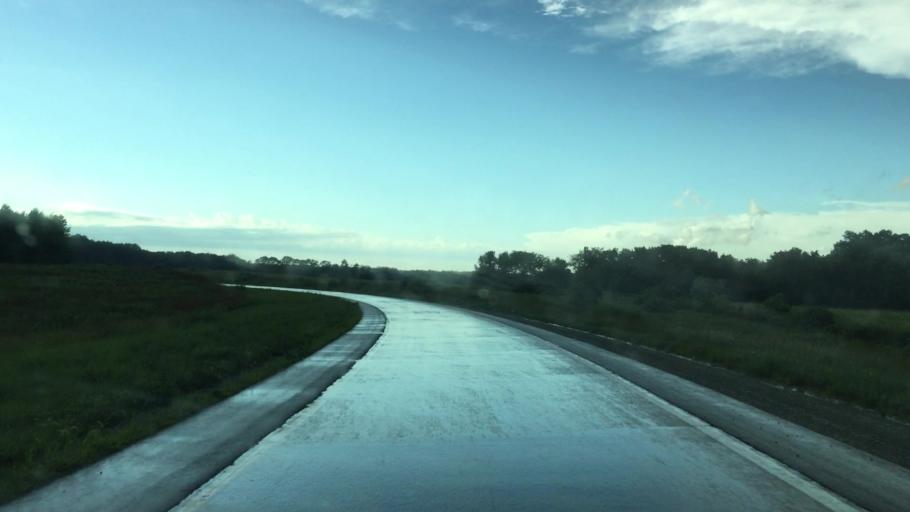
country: US
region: Iowa
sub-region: Henry County
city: Mount Pleasant
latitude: 40.9981
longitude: -91.5442
